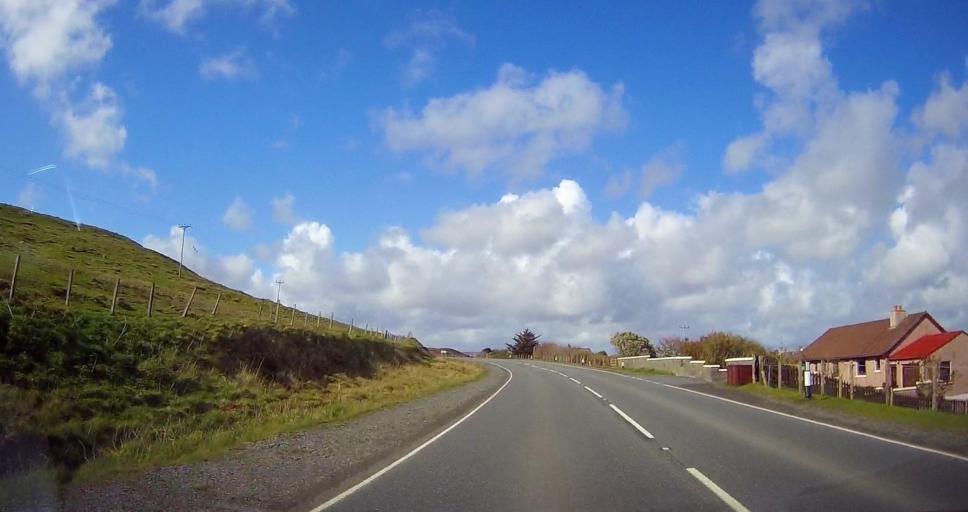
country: GB
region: Scotland
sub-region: Shetland Islands
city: Lerwick
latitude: 60.2394
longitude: -1.2292
